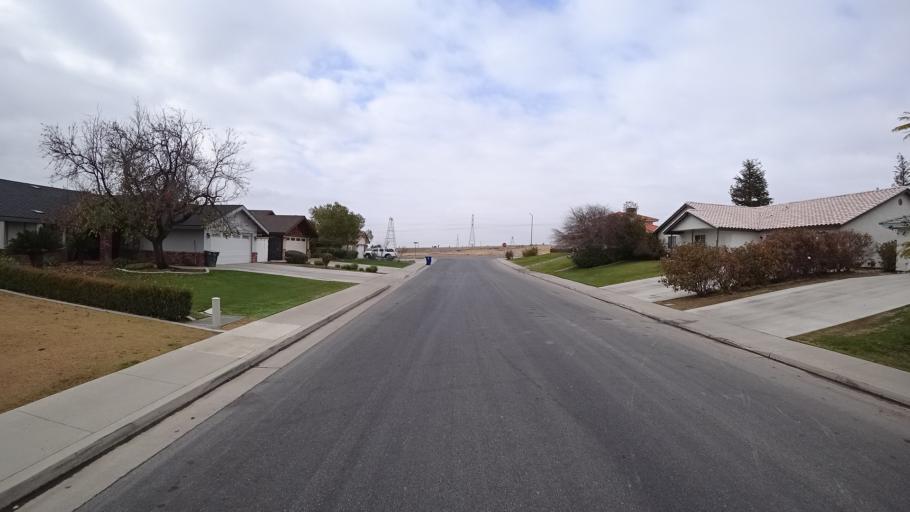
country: US
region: California
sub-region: Kern County
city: Bakersfield
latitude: 35.3821
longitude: -118.9178
